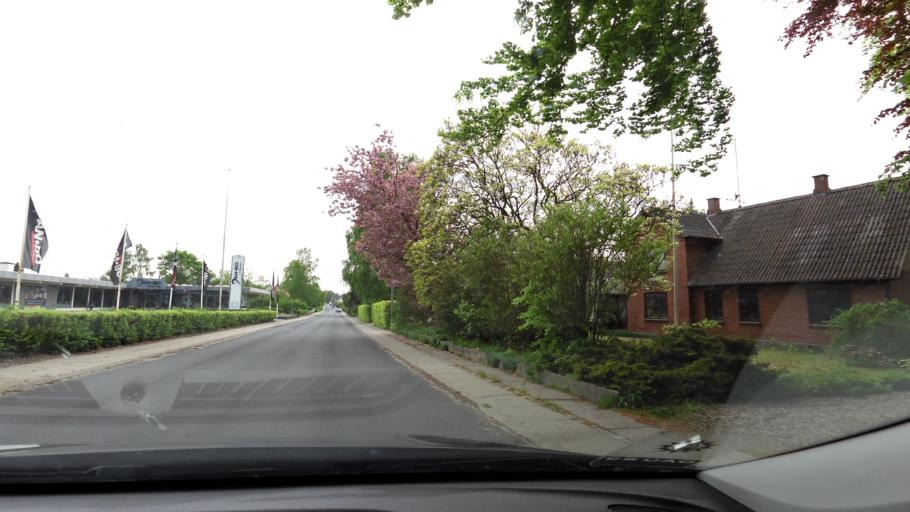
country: DK
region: South Denmark
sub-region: Svendborg Kommune
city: Thuro By
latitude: 55.1731
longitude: 10.7406
